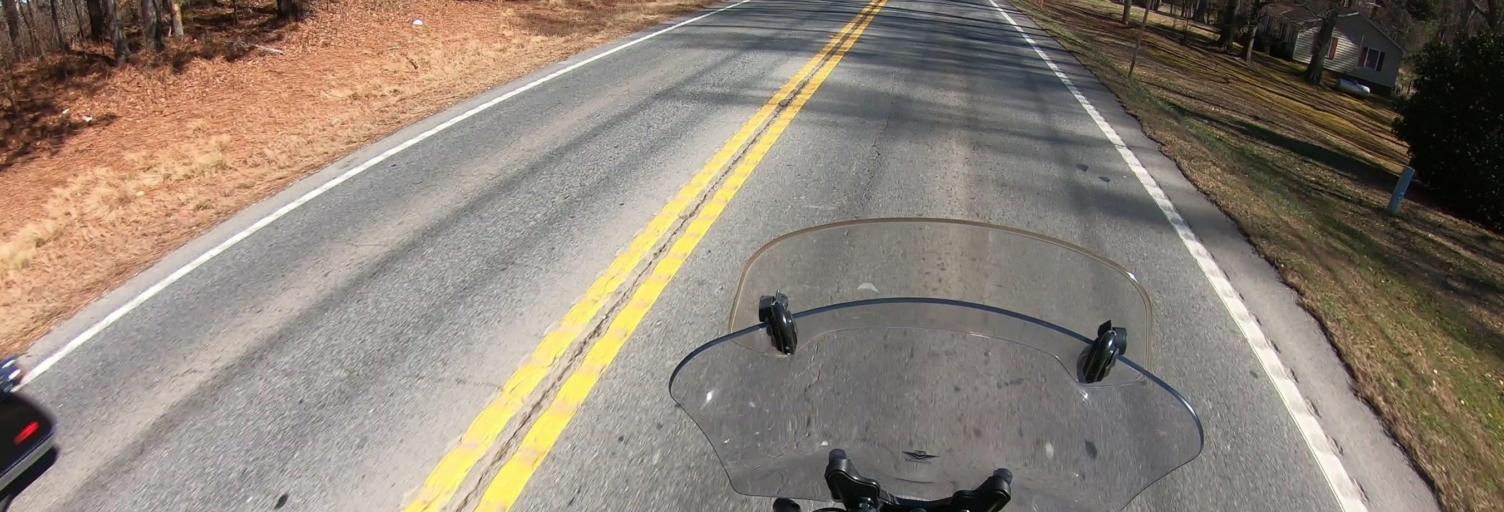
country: US
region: Georgia
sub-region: Forsyth County
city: Cumming
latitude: 34.2970
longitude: -84.1607
